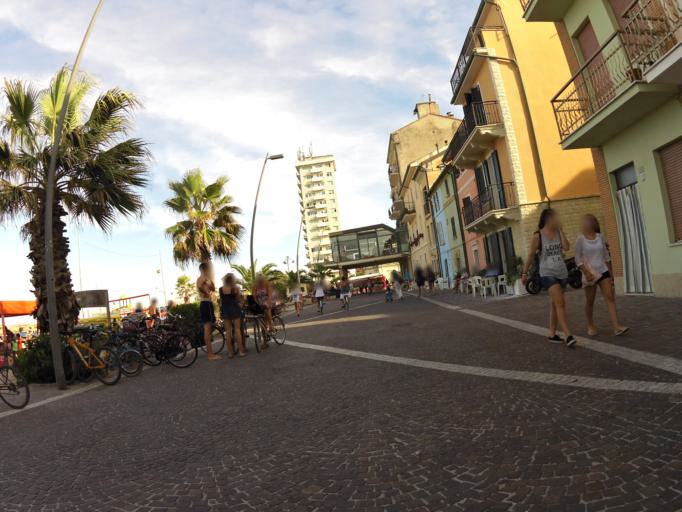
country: IT
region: The Marches
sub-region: Provincia di Macerata
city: Porto Recanati
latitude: 43.4368
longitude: 13.6630
